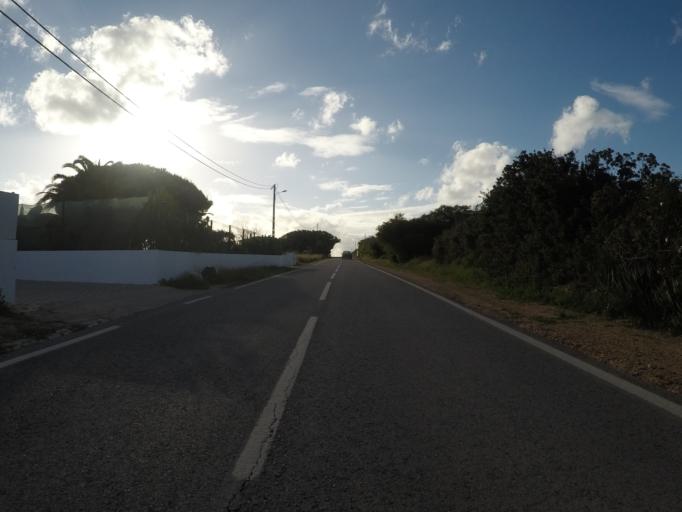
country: PT
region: Faro
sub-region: Lagoa
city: Carvoeiro
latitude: 37.0965
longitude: -8.4386
